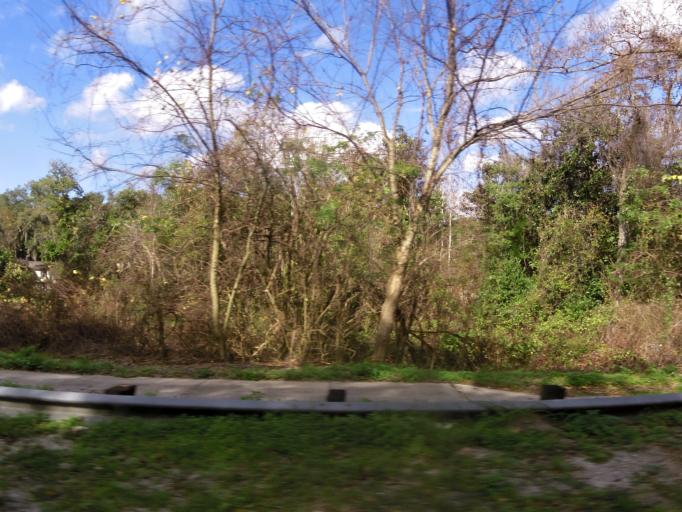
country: US
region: Florida
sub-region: Duval County
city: Atlantic Beach
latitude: 30.3795
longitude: -81.4994
